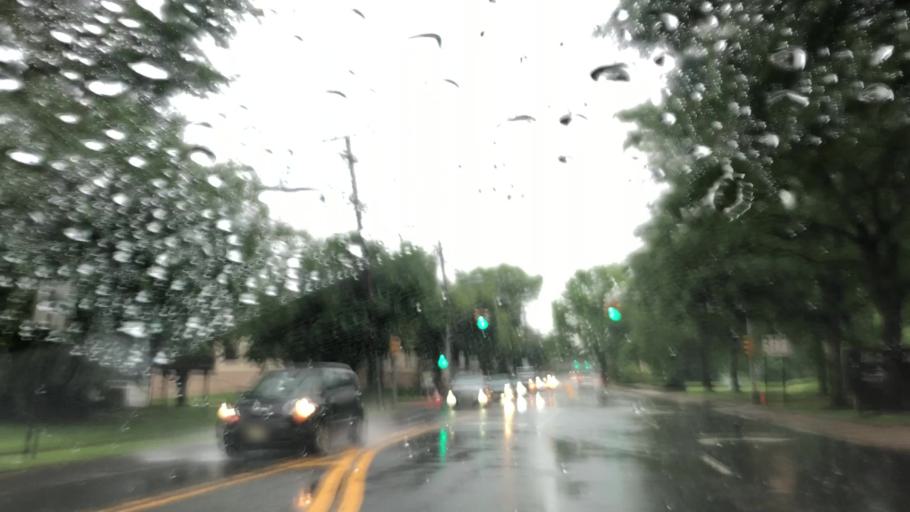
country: US
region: New Jersey
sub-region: Bergen County
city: Rochelle Park
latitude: 40.9119
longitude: -74.0772
